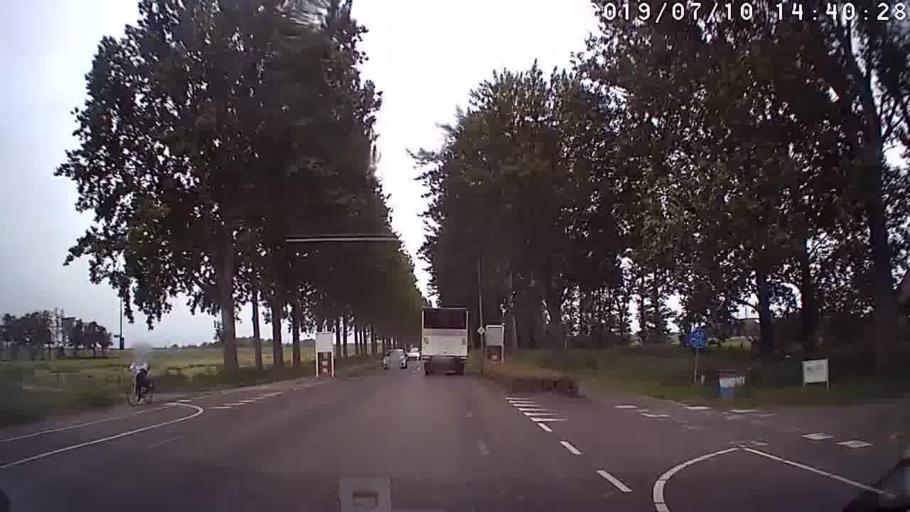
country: NL
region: Gelderland
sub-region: Gemeente Hattem
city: Hattem
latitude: 52.4923
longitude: 6.0474
